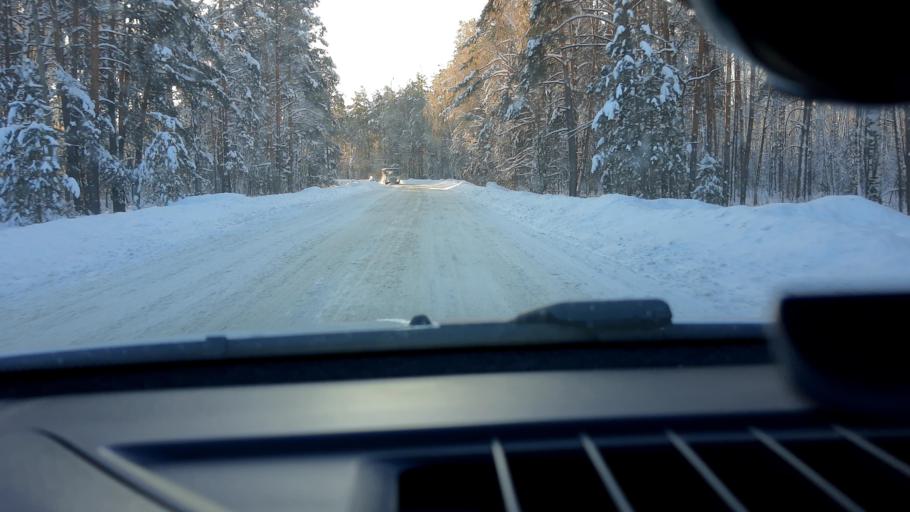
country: RU
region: Nizjnij Novgorod
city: Babino
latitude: 56.3331
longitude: 43.6190
